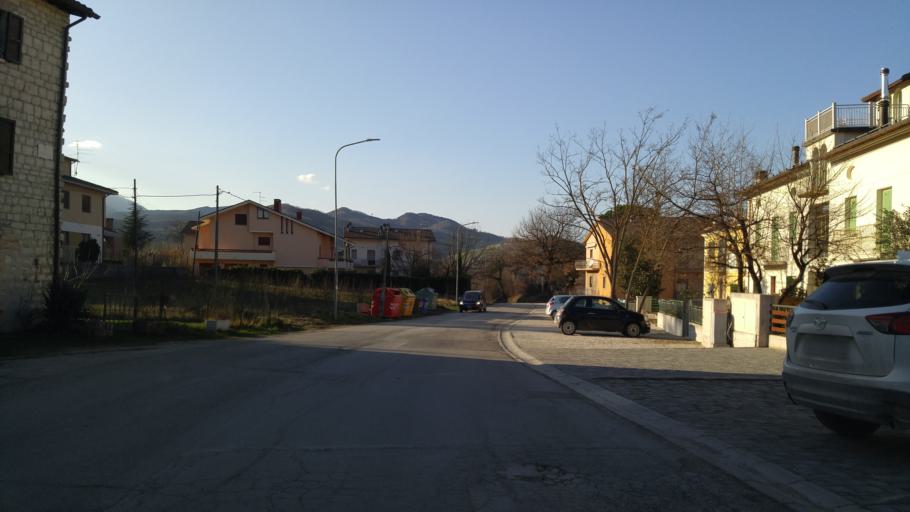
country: IT
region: The Marches
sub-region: Provincia di Pesaro e Urbino
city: Cagli
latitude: 43.5474
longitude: 12.6584
